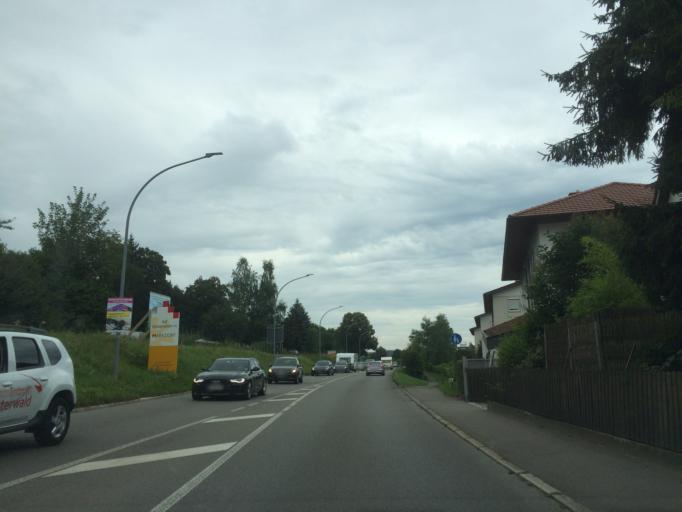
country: DE
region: Baden-Wuerttemberg
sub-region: Tuebingen Region
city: Markdorf
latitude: 47.7188
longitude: 9.3970
